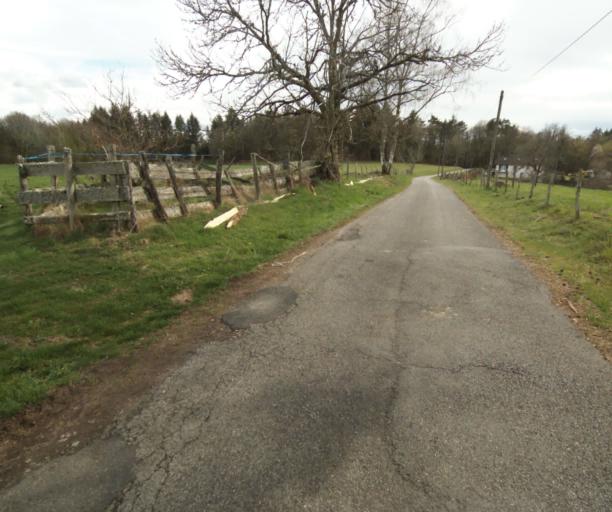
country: FR
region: Limousin
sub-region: Departement de la Correze
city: Argentat
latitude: 45.2113
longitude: 1.9585
